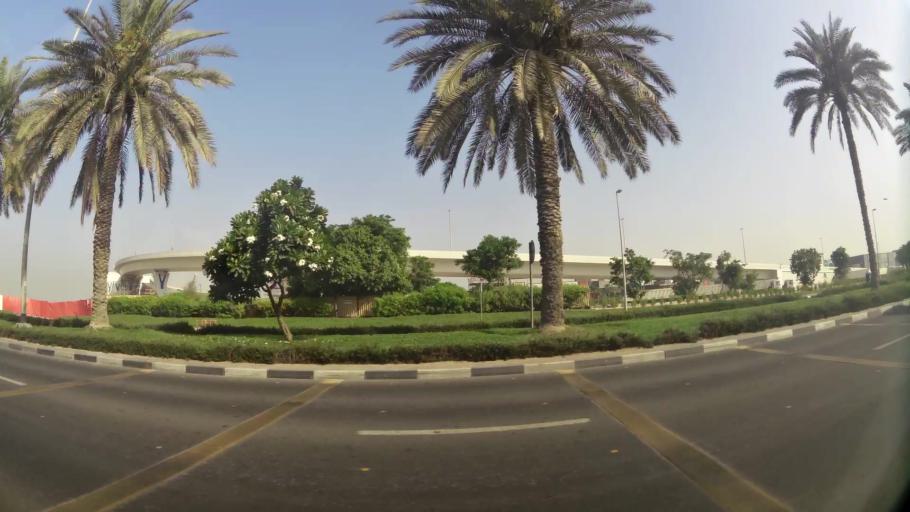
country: AE
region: Ash Shariqah
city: Sharjah
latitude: 25.2893
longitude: 55.3241
